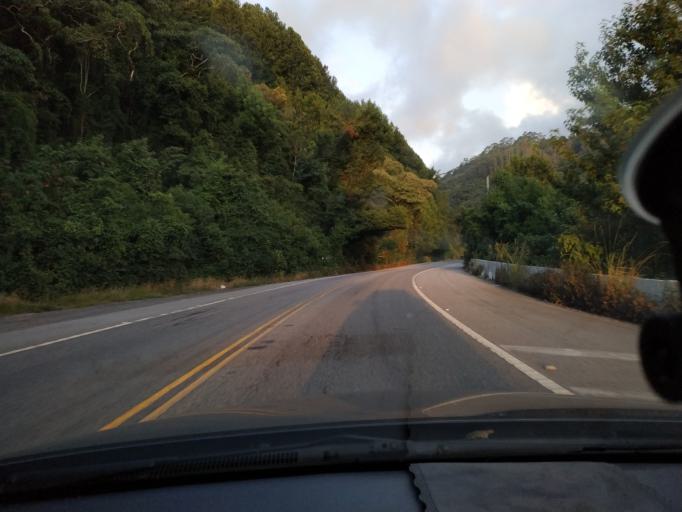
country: BR
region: Sao Paulo
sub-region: Campos Do Jordao
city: Campos do Jordao
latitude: -22.7773
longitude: -45.6144
